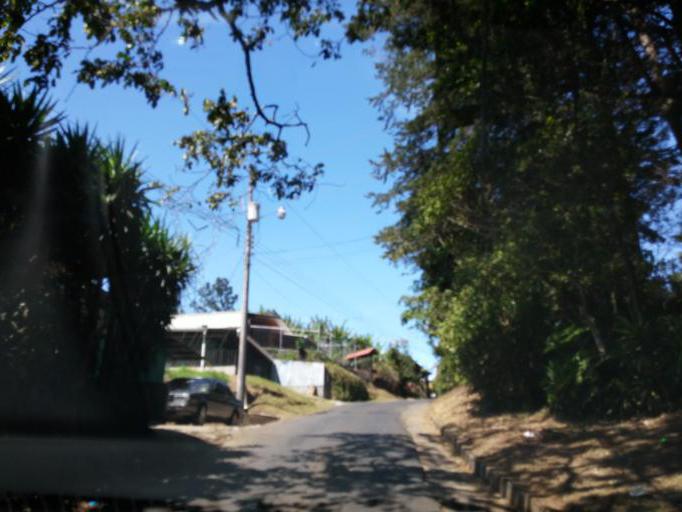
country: CR
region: Heredia
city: Santo Domingo
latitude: 10.0743
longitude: -84.1271
